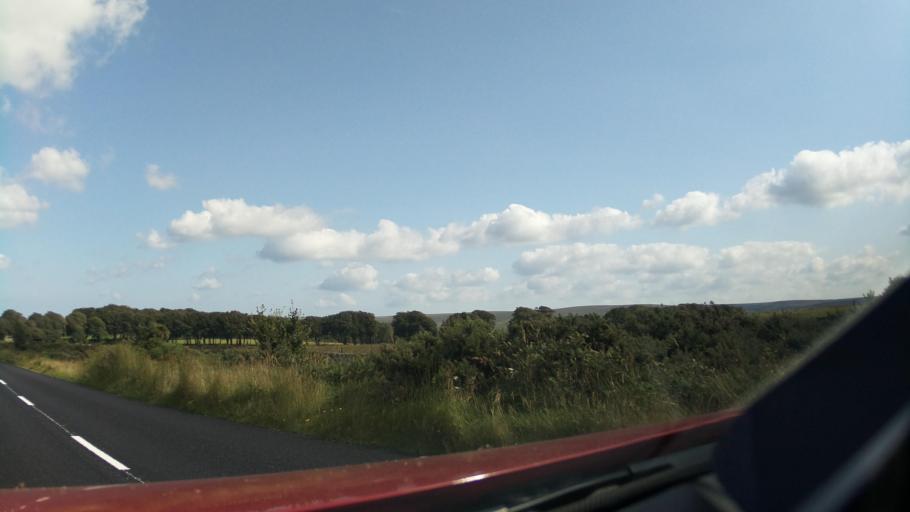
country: GB
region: England
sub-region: Devon
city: Yelverton
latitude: 50.5562
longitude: -3.9490
